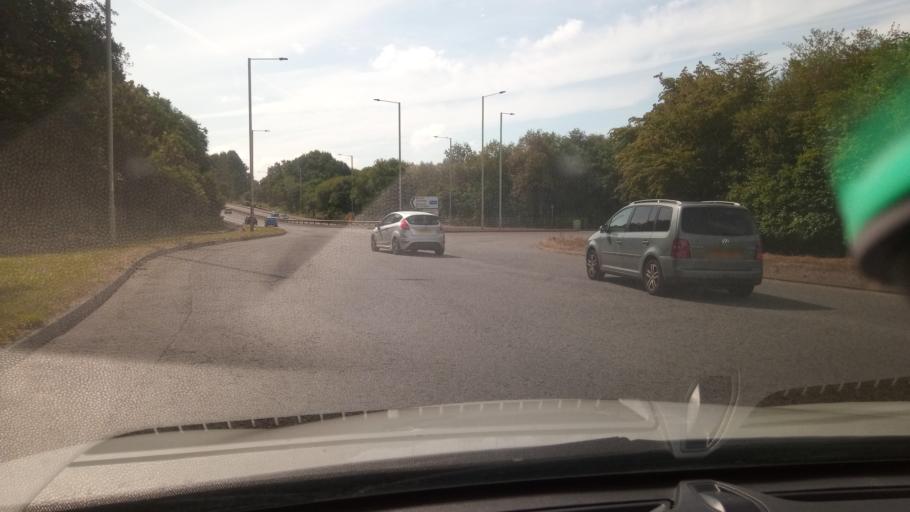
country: GB
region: Wales
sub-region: Rhondda Cynon Taf
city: Llantrisant
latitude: 51.5432
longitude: -3.3875
